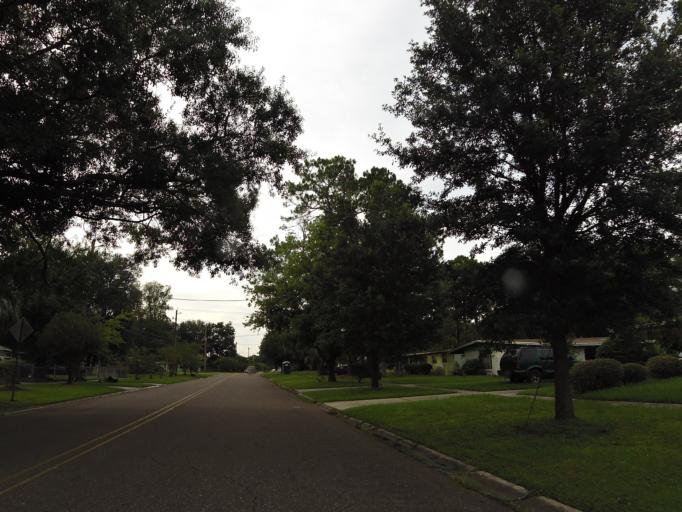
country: US
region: Florida
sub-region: Duval County
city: Jacksonville
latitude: 30.3996
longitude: -81.7196
